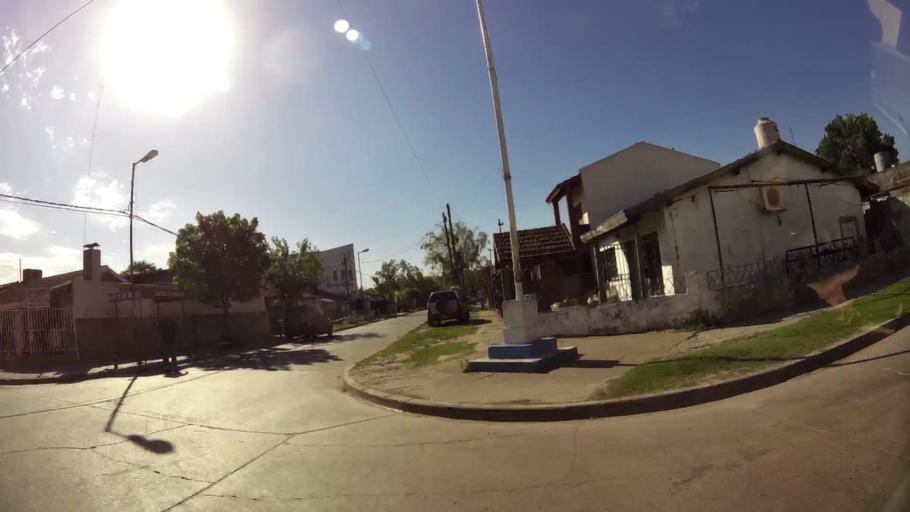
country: AR
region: Buenos Aires
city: Hurlingham
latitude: -34.5546
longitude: -58.6069
